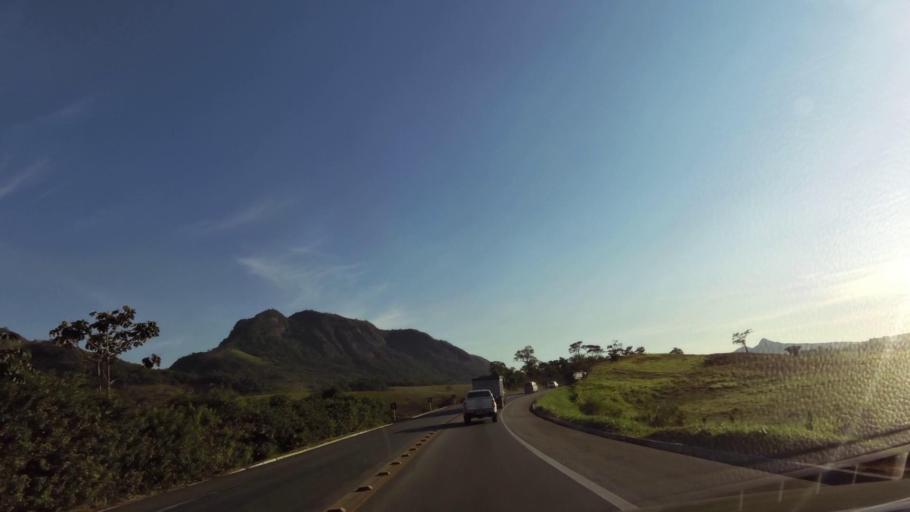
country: BR
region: Espirito Santo
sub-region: Guarapari
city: Guarapari
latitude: -20.6083
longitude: -40.5096
